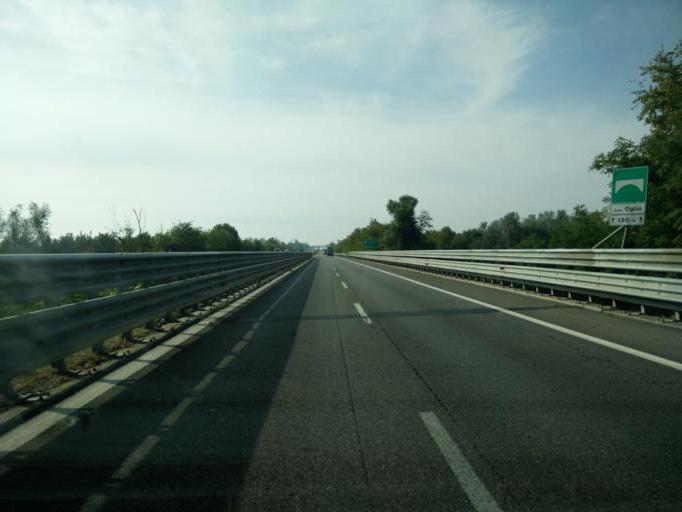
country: IT
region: Lombardy
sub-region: Provincia di Brescia
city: Alfianello
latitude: 45.2478
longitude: 10.1213
